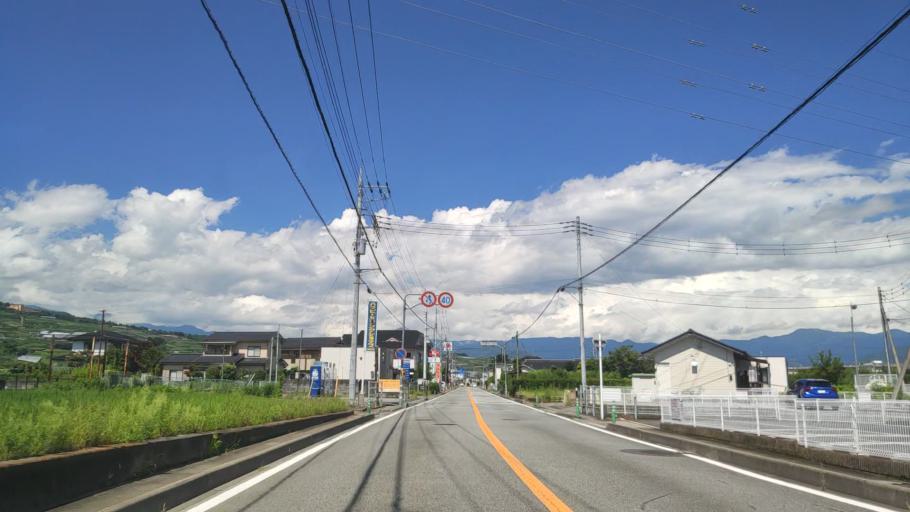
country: JP
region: Yamanashi
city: Isawa
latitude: 35.6785
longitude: 138.6584
